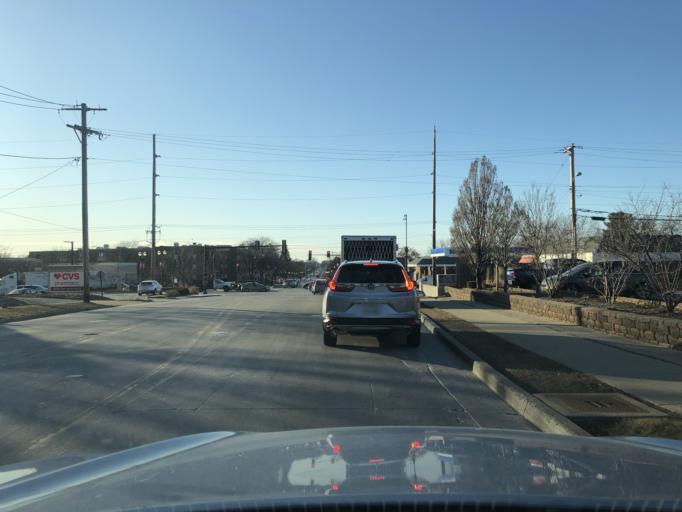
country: US
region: Illinois
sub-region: Cook County
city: Barrington
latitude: 42.1542
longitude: -88.1271
